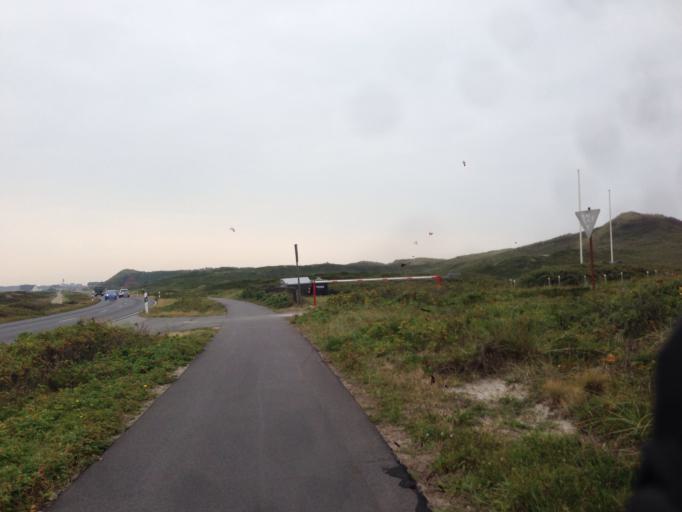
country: DE
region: Schleswig-Holstein
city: Norddorf
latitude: 54.7787
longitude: 8.2841
